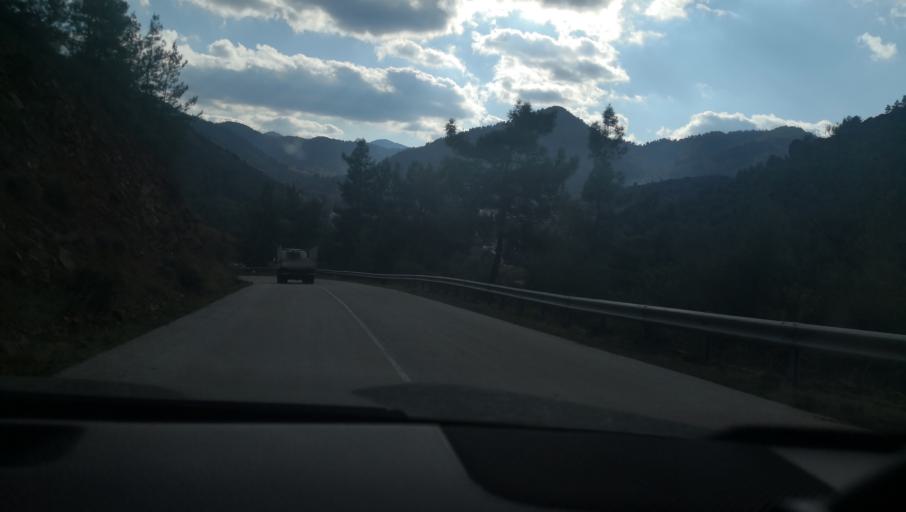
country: CY
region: Lefkosia
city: Lefka
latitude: 35.0485
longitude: 32.7380
